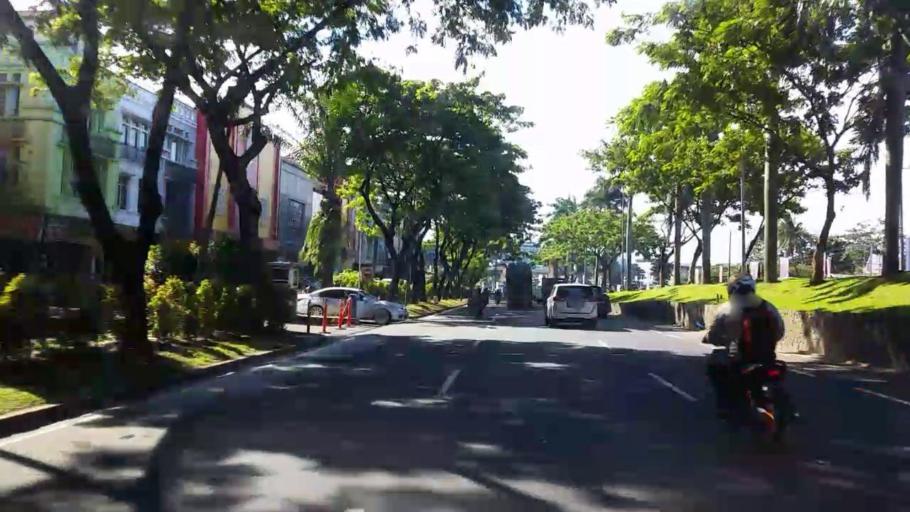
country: ID
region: West Java
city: Serpong
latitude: -6.3027
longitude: 106.6686
